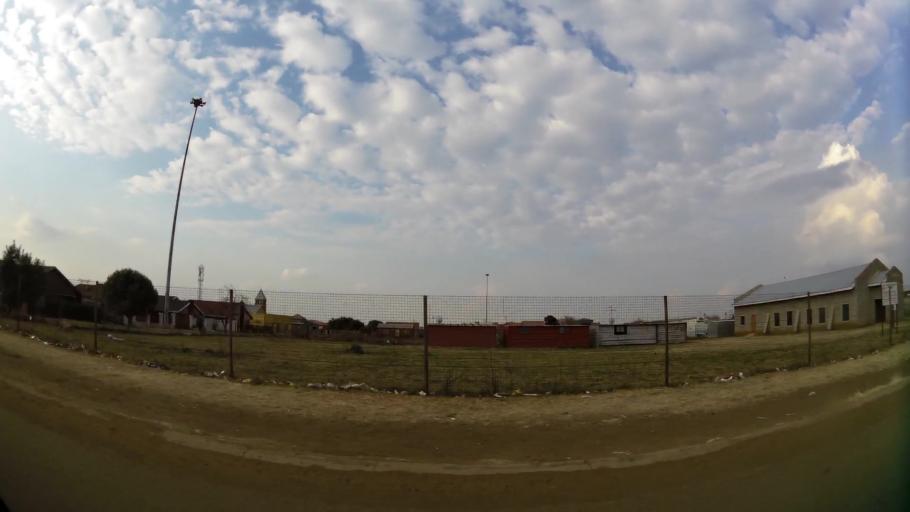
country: ZA
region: Gauteng
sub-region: Sedibeng District Municipality
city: Vanderbijlpark
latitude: -26.6815
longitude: 27.8716
